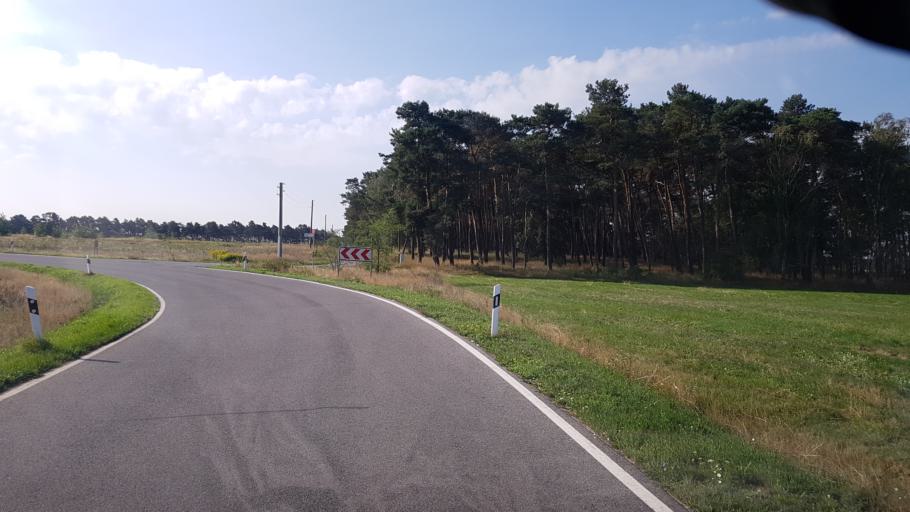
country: DE
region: Brandenburg
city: Luebben
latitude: 51.8843
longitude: 13.8099
